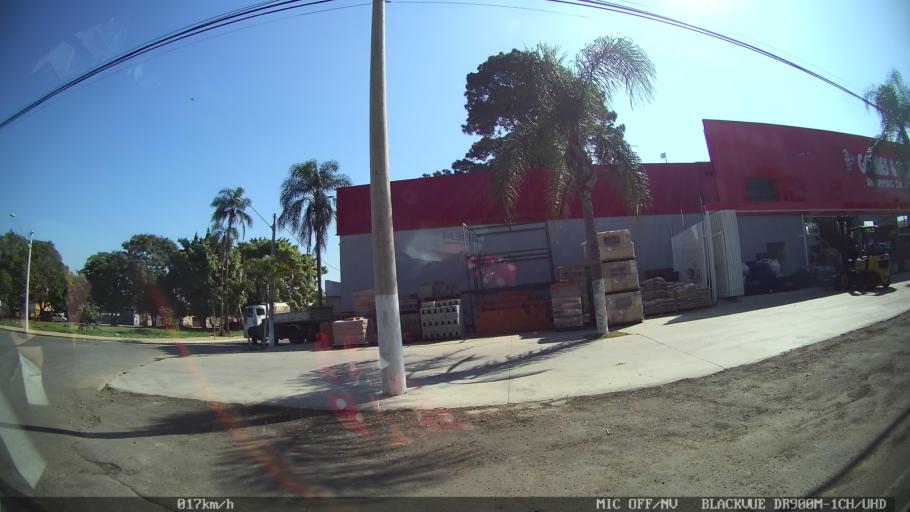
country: BR
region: Sao Paulo
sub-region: Indaiatuba
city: Indaiatuba
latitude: -23.0344
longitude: -47.1058
